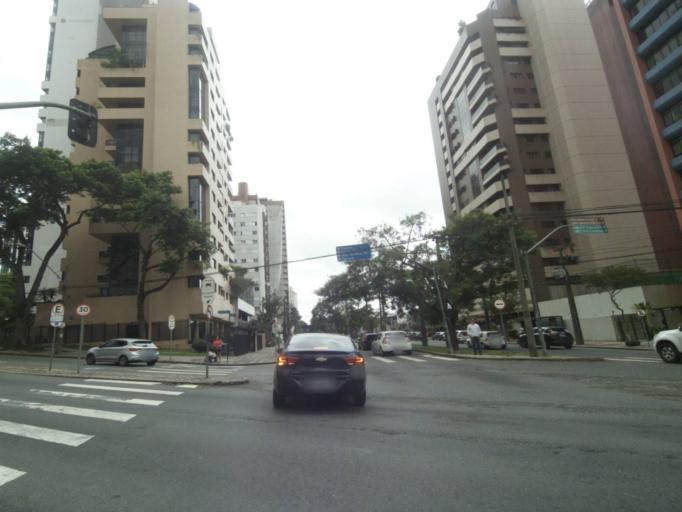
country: BR
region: Parana
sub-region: Curitiba
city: Curitiba
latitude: -25.4472
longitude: -49.2877
